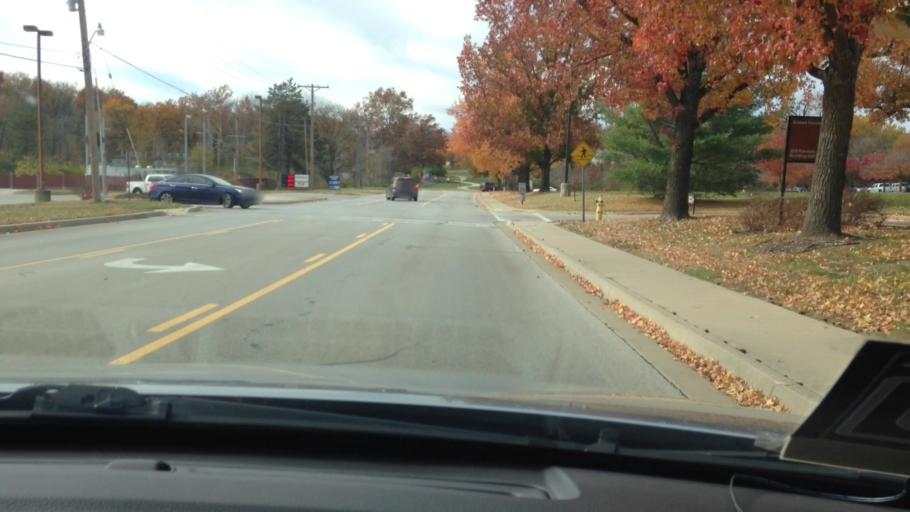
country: US
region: Kansas
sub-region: Leavenworth County
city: Leavenworth
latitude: 39.3383
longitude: -94.9232
